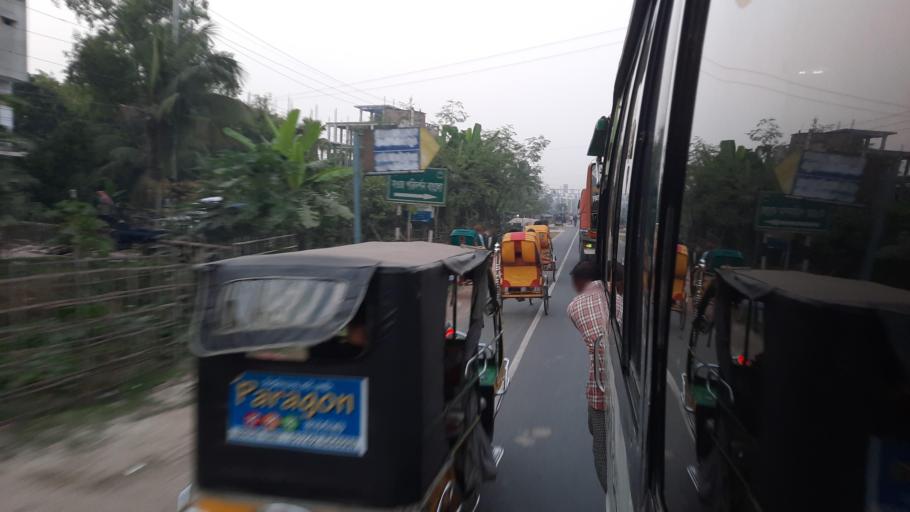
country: BD
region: Khulna
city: Jessore
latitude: 23.1673
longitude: 89.1932
